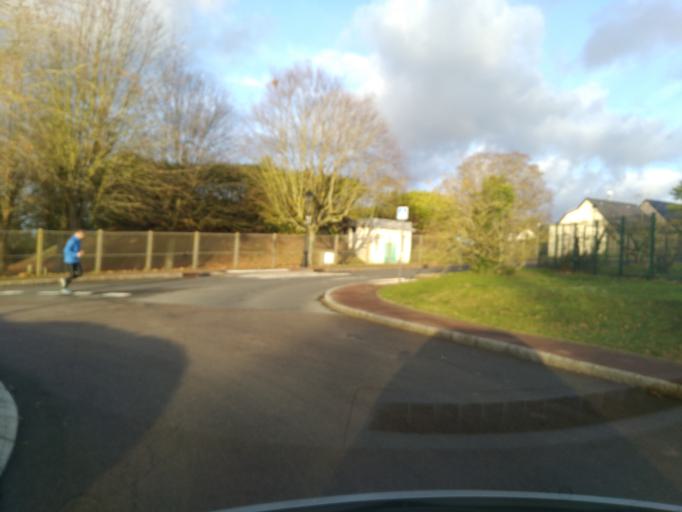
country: FR
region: Ile-de-France
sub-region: Departement des Yvelines
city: Chambourcy
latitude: 48.9026
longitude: 2.0319
